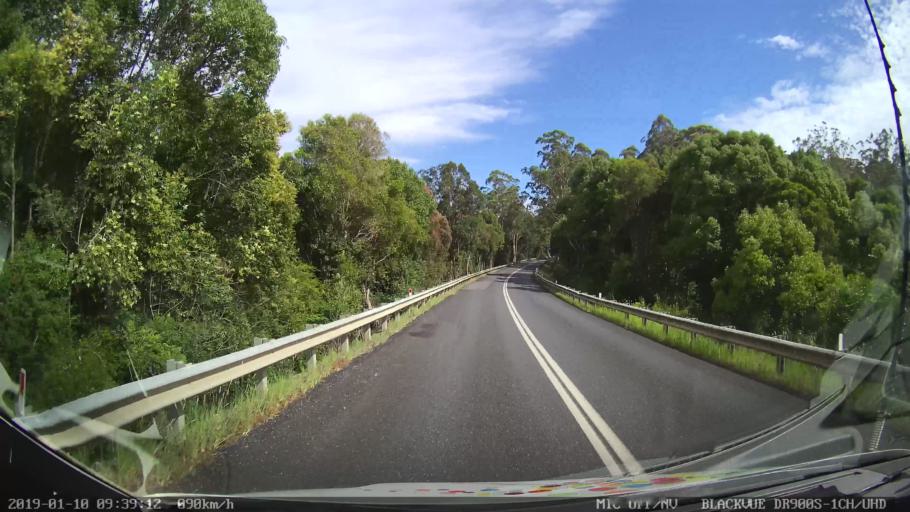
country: AU
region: New South Wales
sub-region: Coffs Harbour
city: Nana Glen
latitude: -30.1663
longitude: 153.0030
